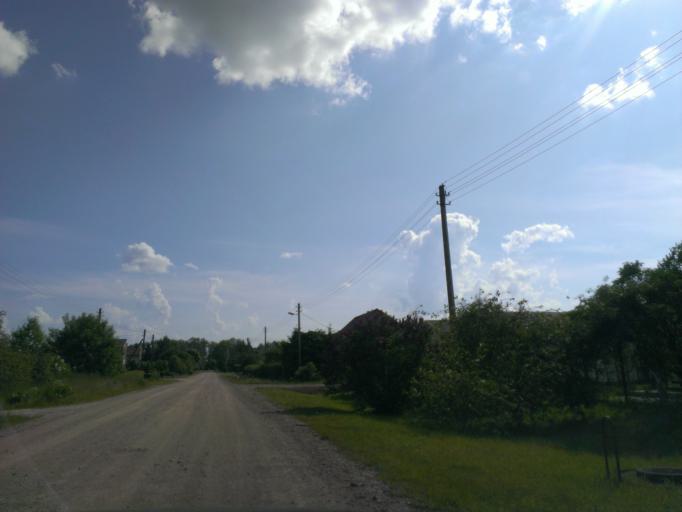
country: LT
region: Klaipedos apskritis
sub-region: Klaipeda
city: Palanga
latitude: 55.9051
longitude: 21.1340
